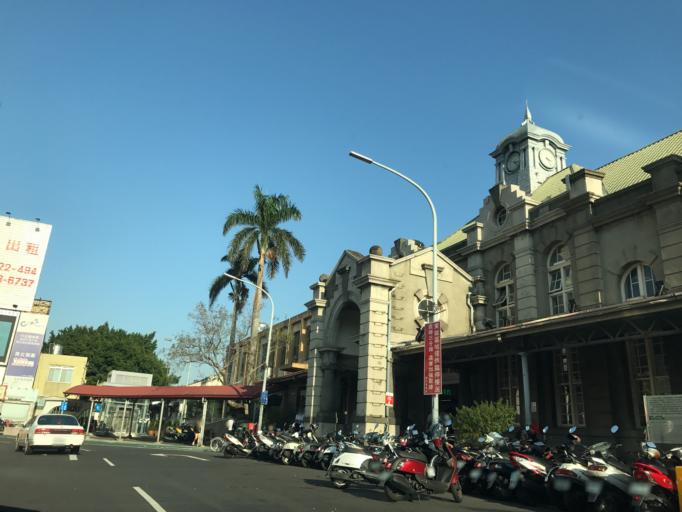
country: TW
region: Taiwan
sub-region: Hsinchu
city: Hsinchu
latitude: 24.8017
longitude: 120.9714
